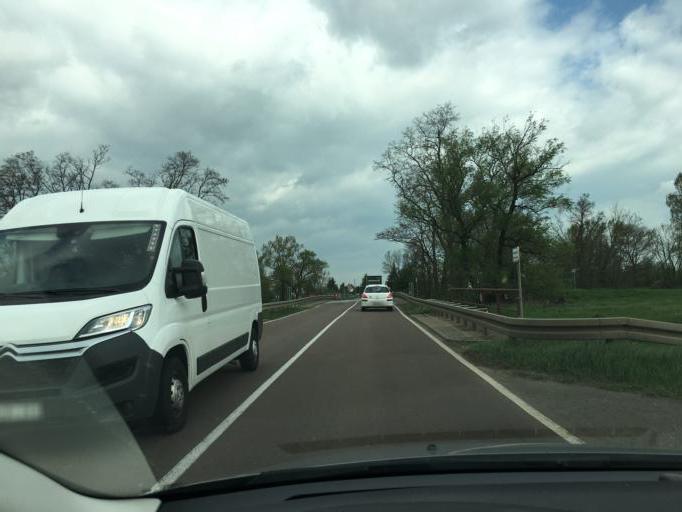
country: DE
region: Saxony-Anhalt
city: Giersleben
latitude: 51.7755
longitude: 11.5854
